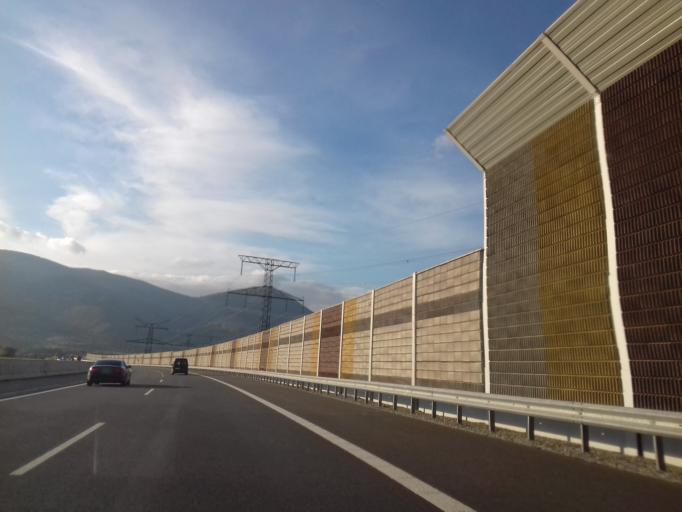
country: SK
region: Zilinsky
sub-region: Okres Zilina
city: Vrutky
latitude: 49.1208
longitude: 18.9345
